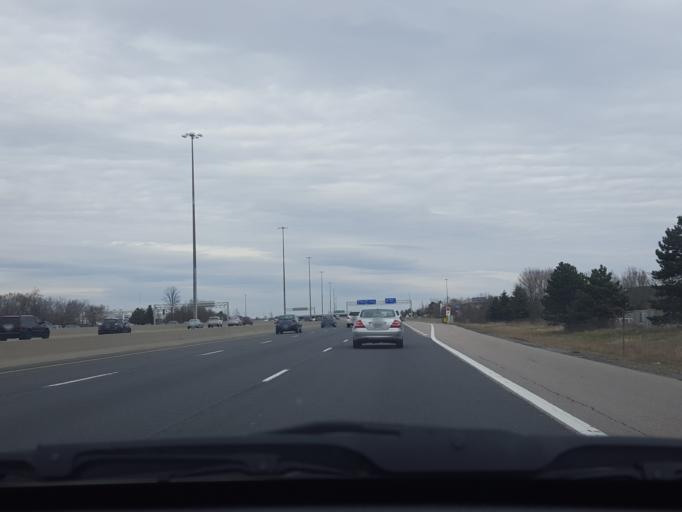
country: CA
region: Ontario
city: Pickering
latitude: 43.8110
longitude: -79.1227
